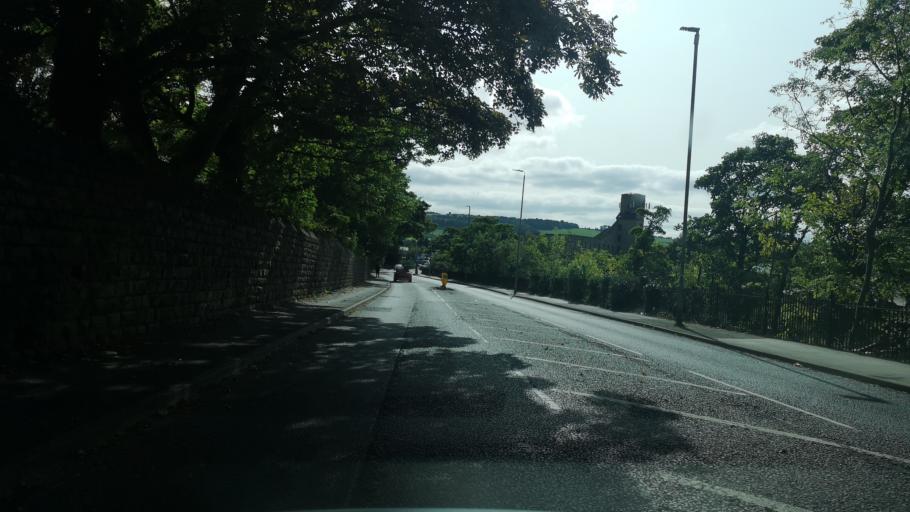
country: GB
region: England
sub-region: Kirklees
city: Dewsbury
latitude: 53.6803
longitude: -1.6356
